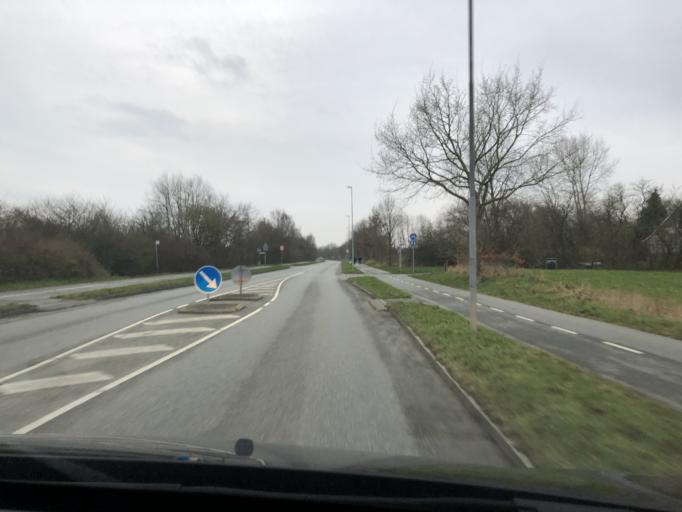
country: DK
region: South Denmark
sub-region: Svendborg Kommune
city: Svendborg
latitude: 55.0833
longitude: 10.6166
